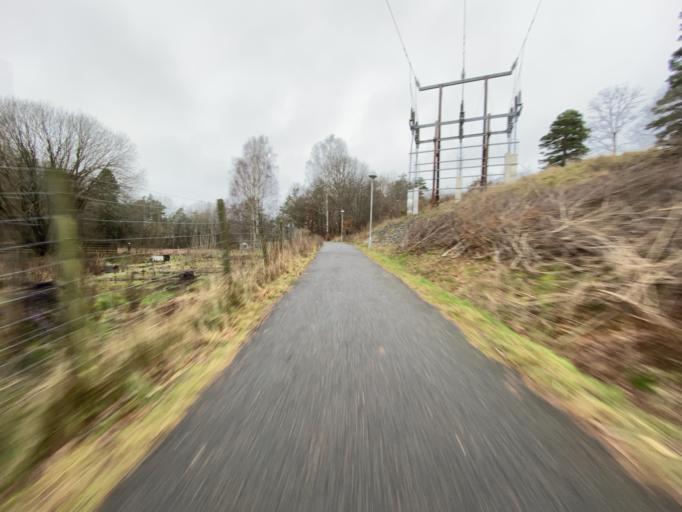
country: SE
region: Vaestra Goetaland
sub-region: Molndal
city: Moelndal
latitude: 57.7092
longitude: 12.0399
